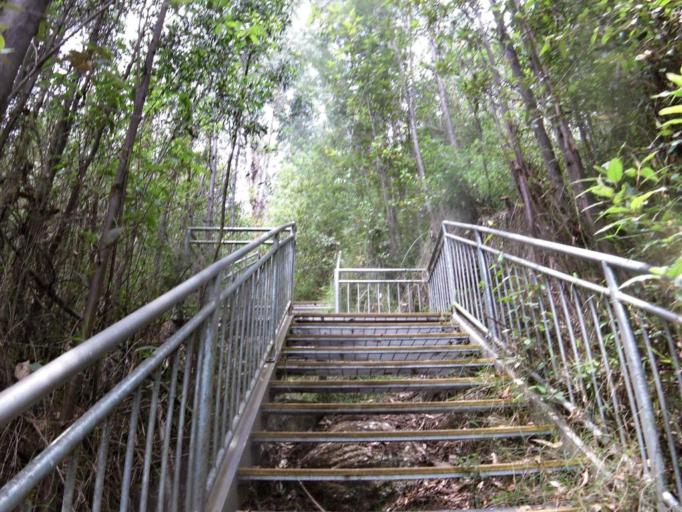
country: AU
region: Victoria
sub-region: Yarra Ranges
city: Healesville
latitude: -37.4576
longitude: 145.5725
